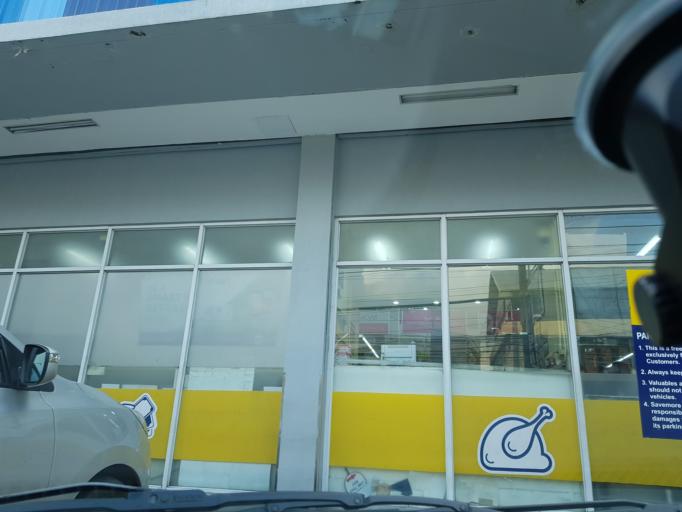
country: PH
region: Metro Manila
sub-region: Quezon City
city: Quezon City
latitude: 14.6360
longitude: 121.0585
